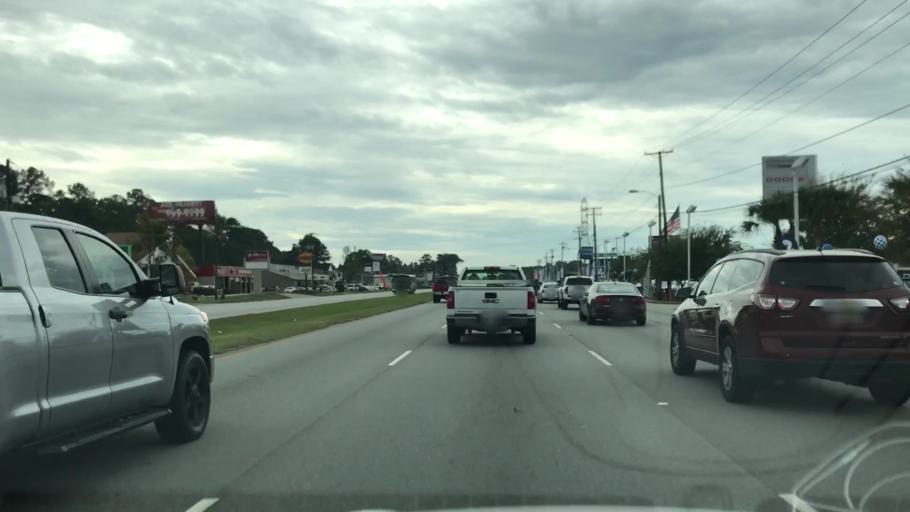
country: US
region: South Carolina
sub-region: Berkeley County
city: Goose Creek
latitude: 32.9599
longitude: -80.0434
